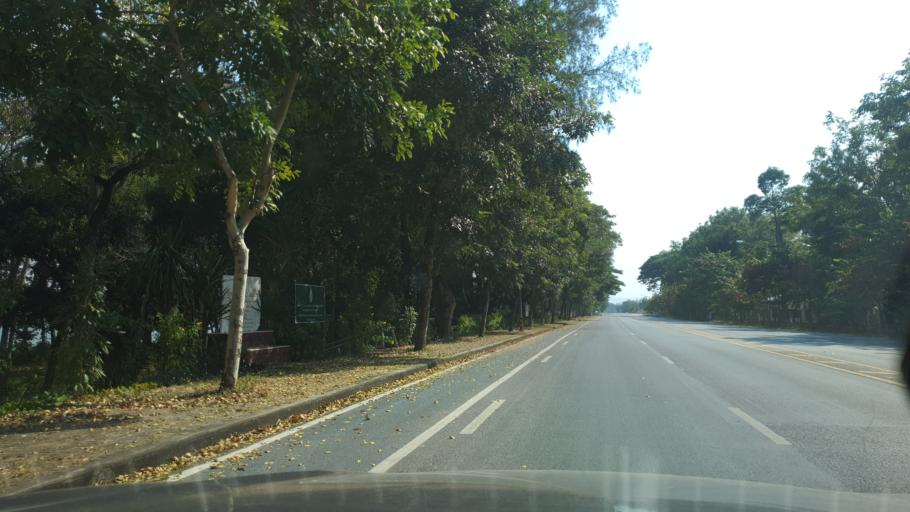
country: TH
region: Tak
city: Tak
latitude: 16.8695
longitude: 99.1190
